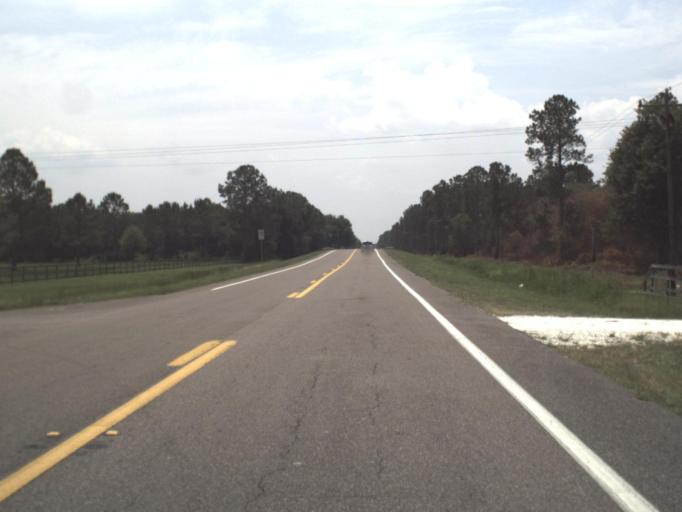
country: US
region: Florida
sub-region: Putnam County
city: Palatka
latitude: 29.5183
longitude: -81.7517
